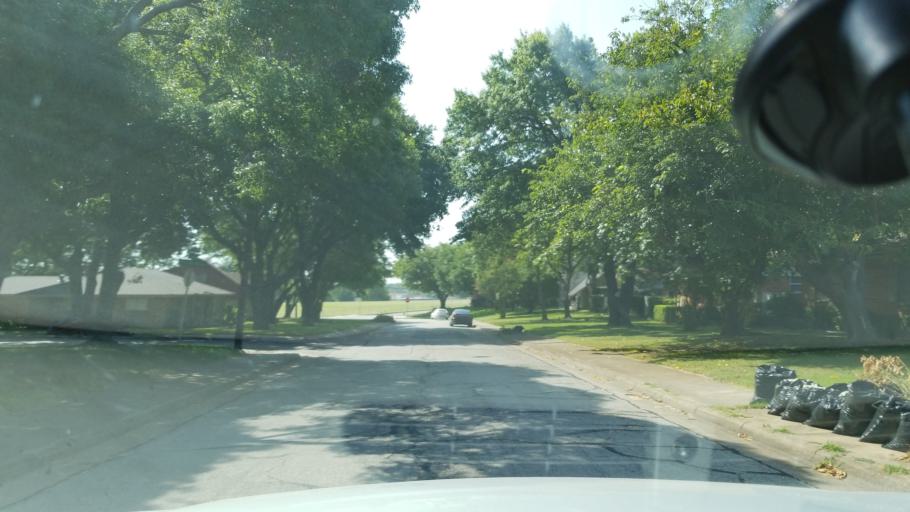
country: US
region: Texas
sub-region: Dallas County
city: Duncanville
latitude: 32.6805
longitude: -96.8453
